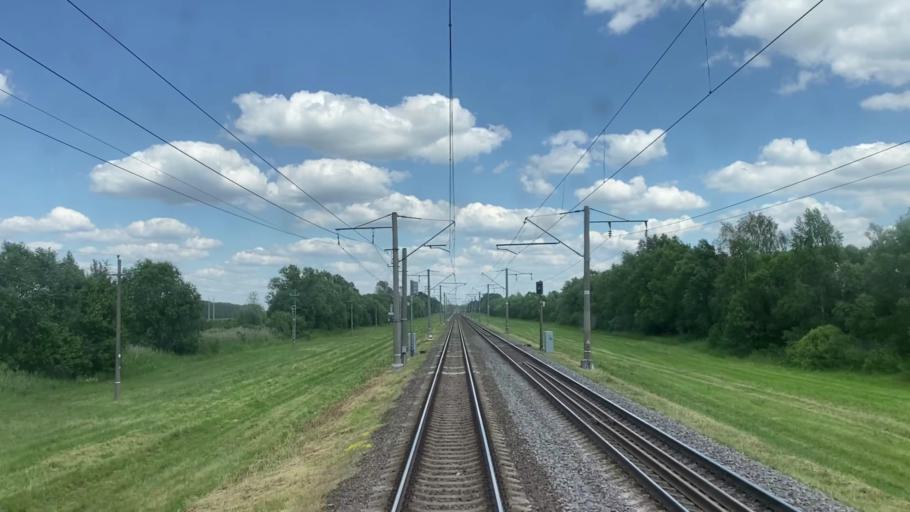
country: BY
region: Brest
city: Zhabinka
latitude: 52.2601
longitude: 24.1350
